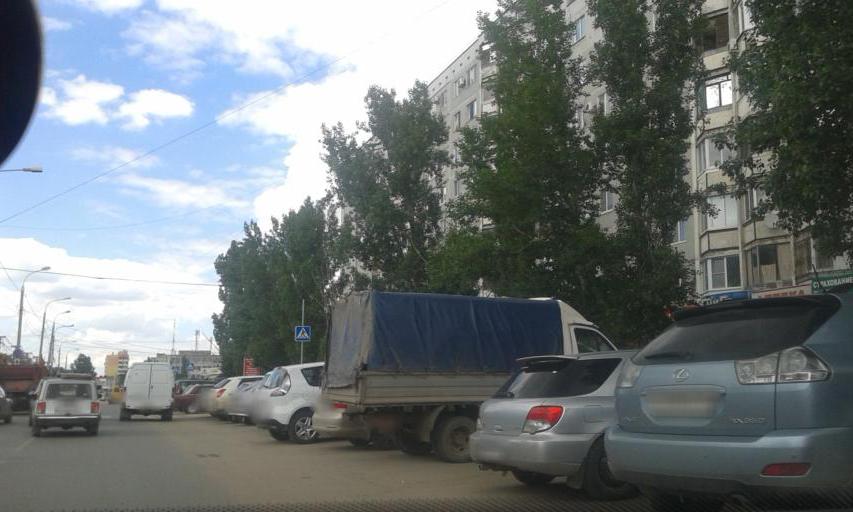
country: RU
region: Volgograd
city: Volgograd
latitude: 48.7566
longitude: 44.5021
